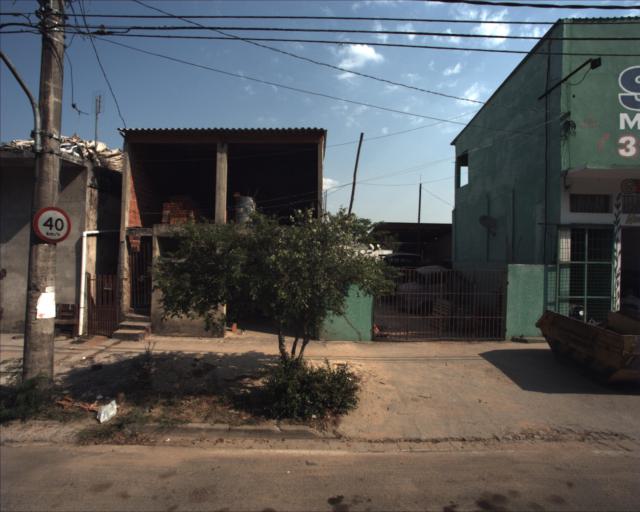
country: BR
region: Sao Paulo
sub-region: Sorocaba
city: Sorocaba
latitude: -23.4336
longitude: -47.4558
